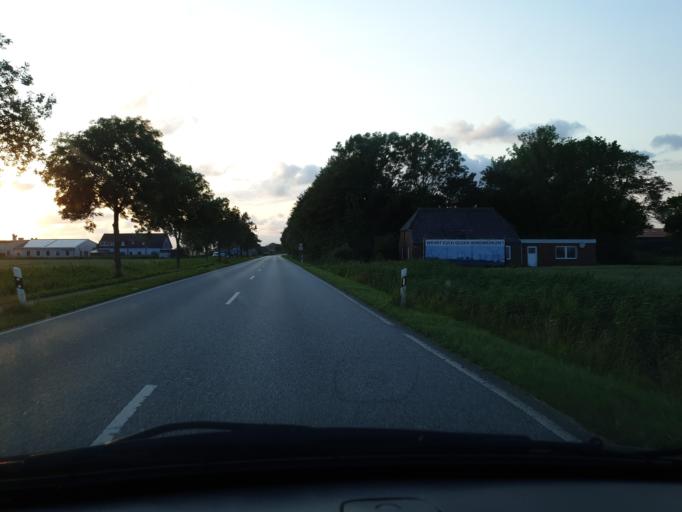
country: DE
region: Schleswig-Holstein
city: Schmedeswurth
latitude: 53.9245
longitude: 9.0424
